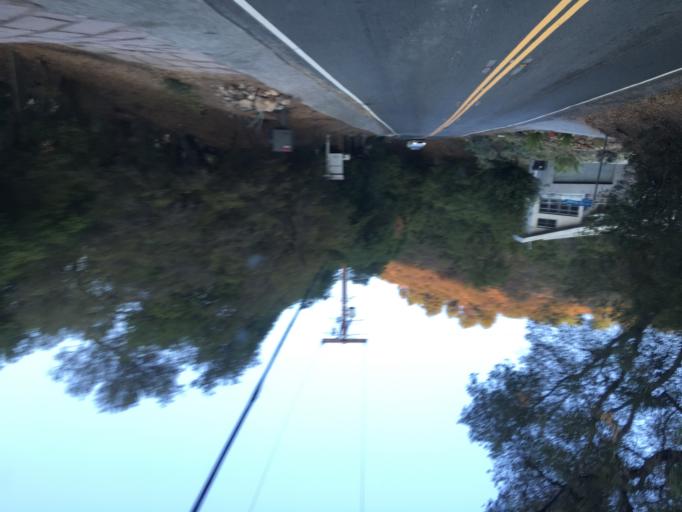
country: US
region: California
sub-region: Los Angeles County
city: Las Flores
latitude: 34.0667
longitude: -118.6423
